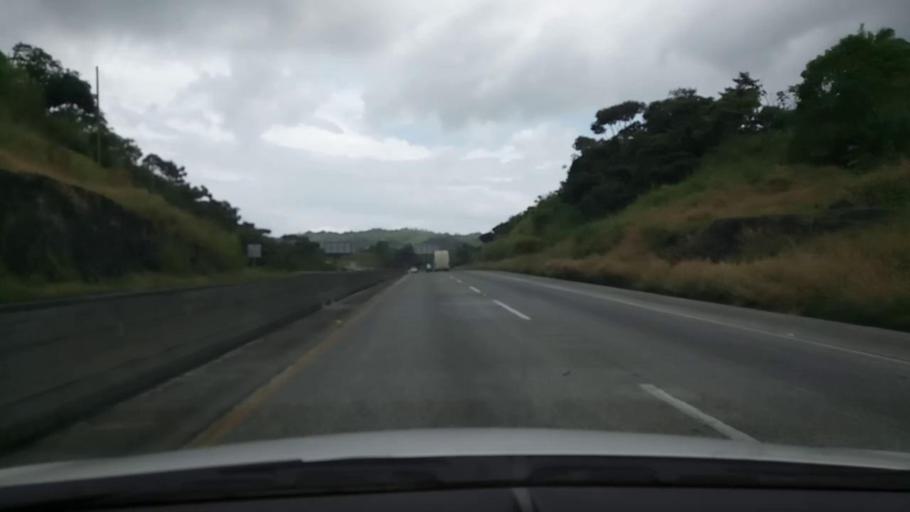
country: PA
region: Colon
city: Gatun
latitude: 9.2812
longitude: -79.7633
